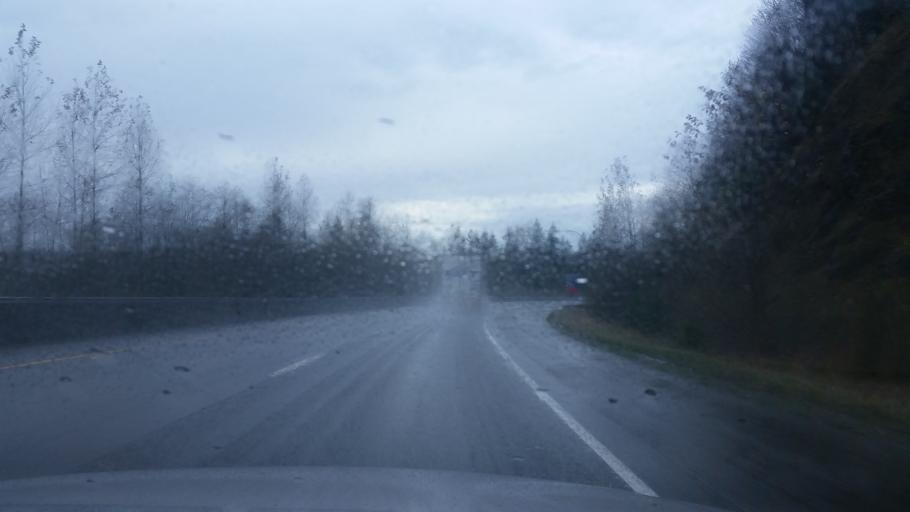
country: US
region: Washington
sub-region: King County
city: Hobart
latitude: 47.4368
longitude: -121.9667
